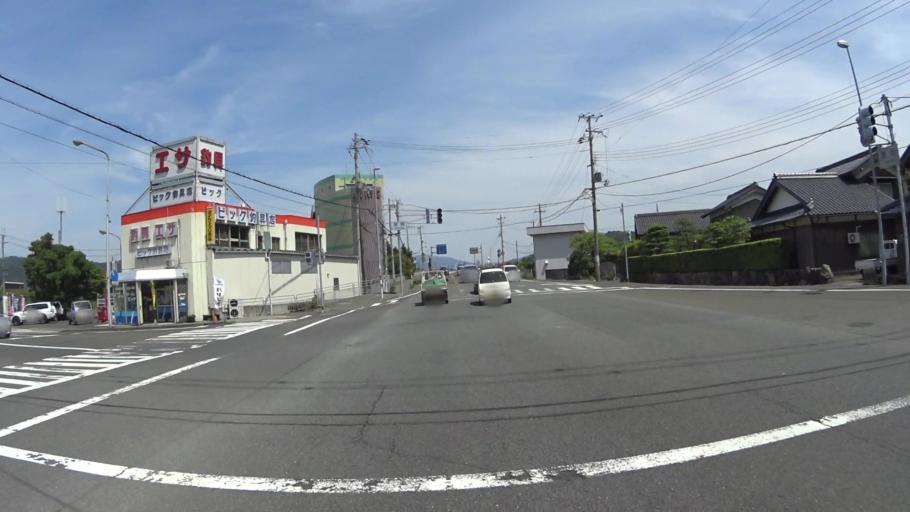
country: JP
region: Fukui
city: Obama
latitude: 35.4894
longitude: 135.7542
